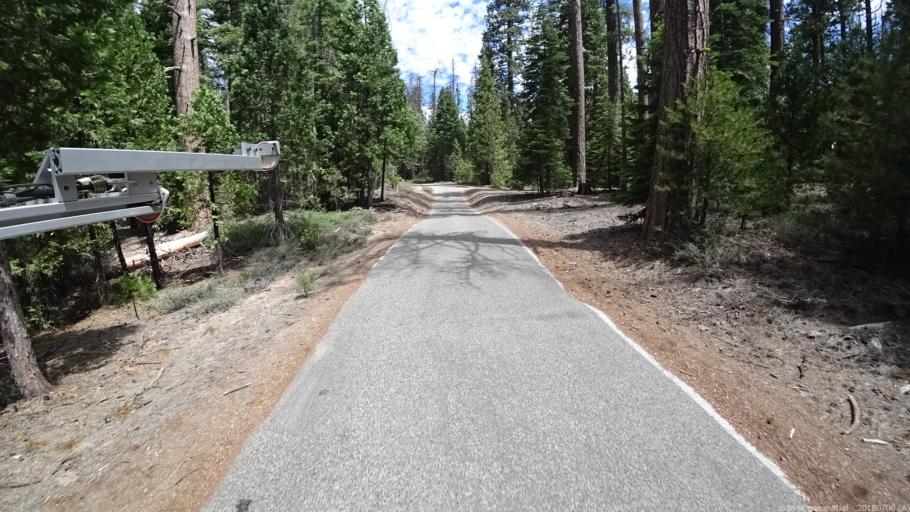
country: US
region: California
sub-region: Madera County
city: Oakhurst
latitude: 37.4067
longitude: -119.4112
